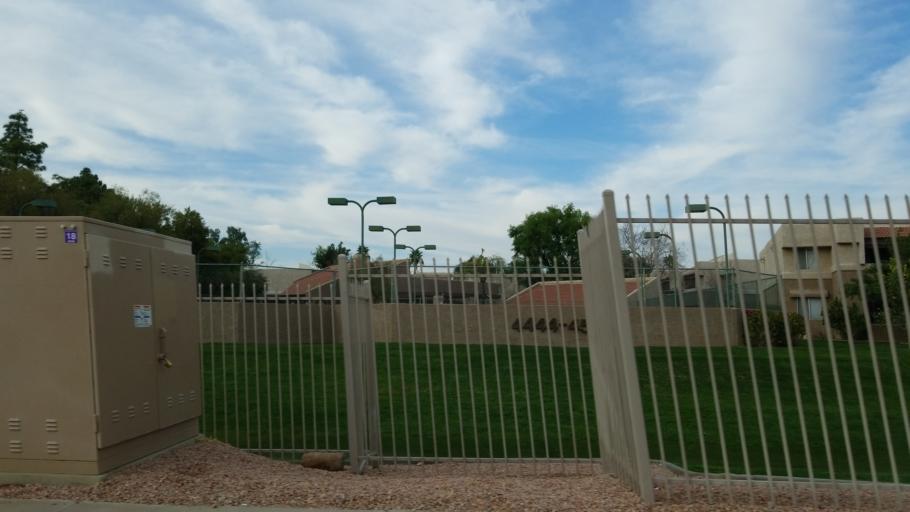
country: US
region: Arizona
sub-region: Maricopa County
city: Paradise Valley
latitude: 33.6051
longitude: -111.9836
